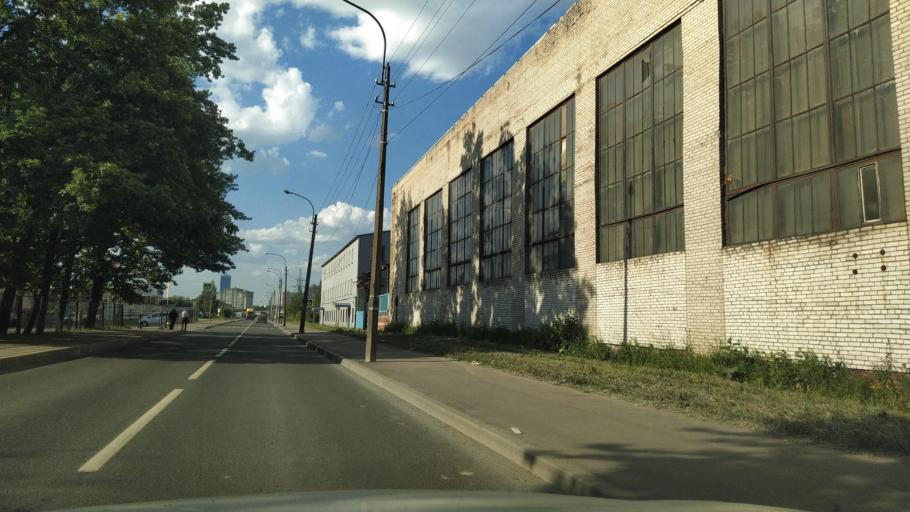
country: RU
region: St.-Petersburg
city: Dachnoye
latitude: 59.8291
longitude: 30.3081
